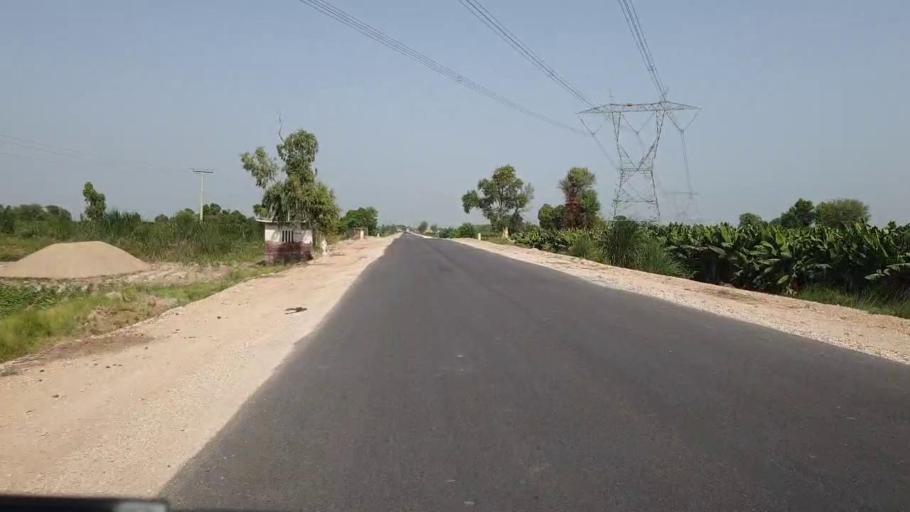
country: PK
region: Sindh
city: Sakrand
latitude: 26.2534
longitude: 68.2018
